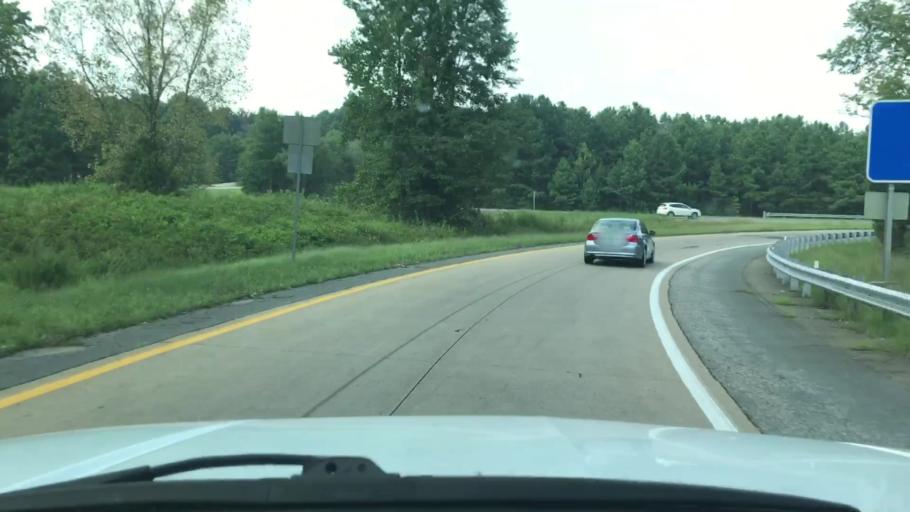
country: US
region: Virginia
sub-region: Hanover County
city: Mechanicsville
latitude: 37.6062
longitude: -77.3625
